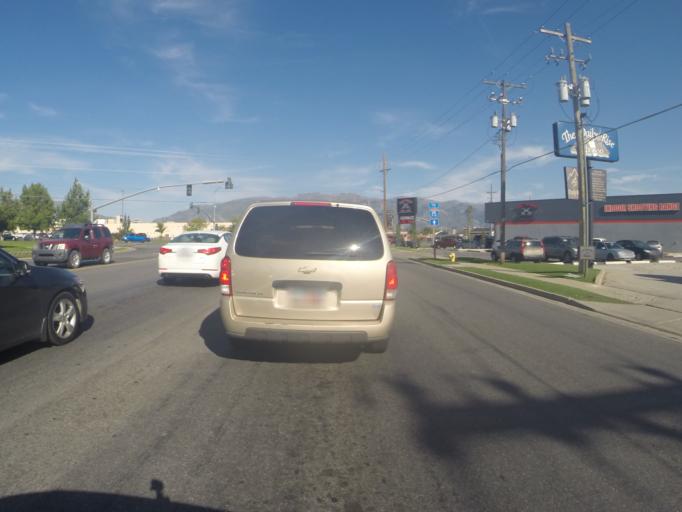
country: US
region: Utah
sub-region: Davis County
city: Clearfield
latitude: 41.0891
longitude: -112.0021
